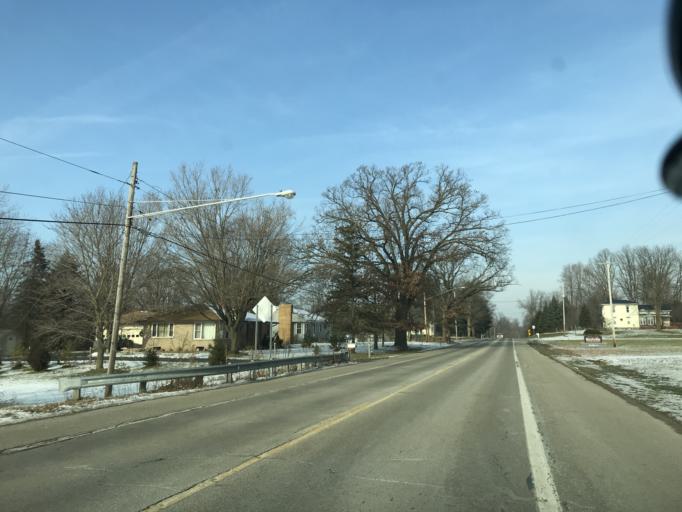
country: US
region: Michigan
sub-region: Barry County
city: Nashville
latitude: 42.5931
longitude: -85.0945
